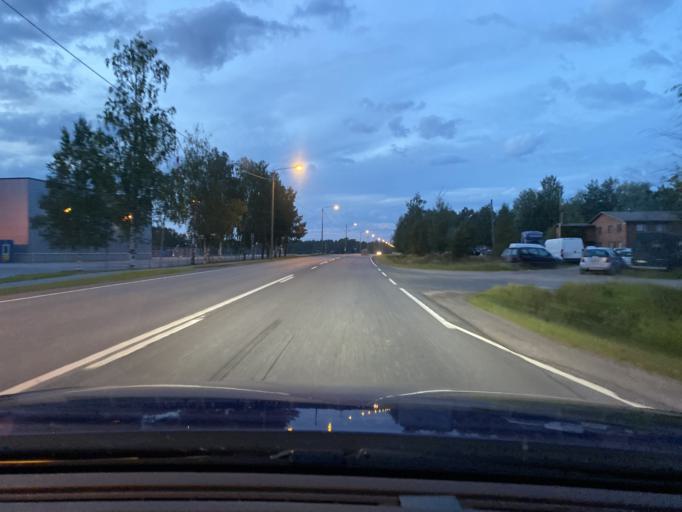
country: FI
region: Southern Ostrobothnia
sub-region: Suupohja
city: Kauhajoki
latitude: 62.4452
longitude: 22.2122
